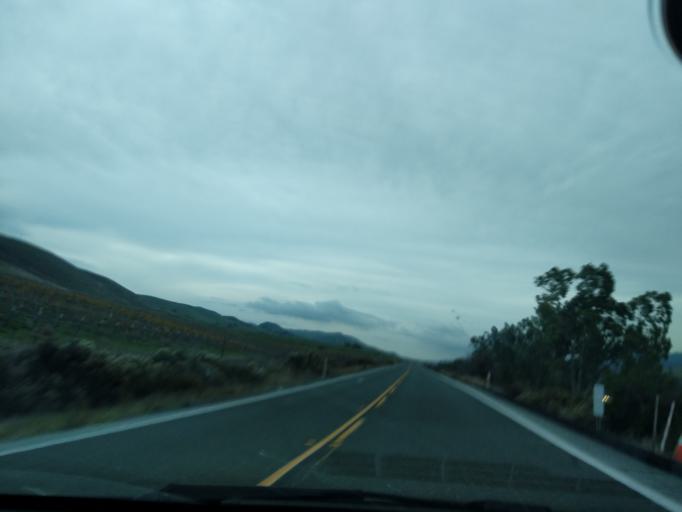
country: US
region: California
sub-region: San Benito County
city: Ridgemark
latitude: 36.7011
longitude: -121.2744
